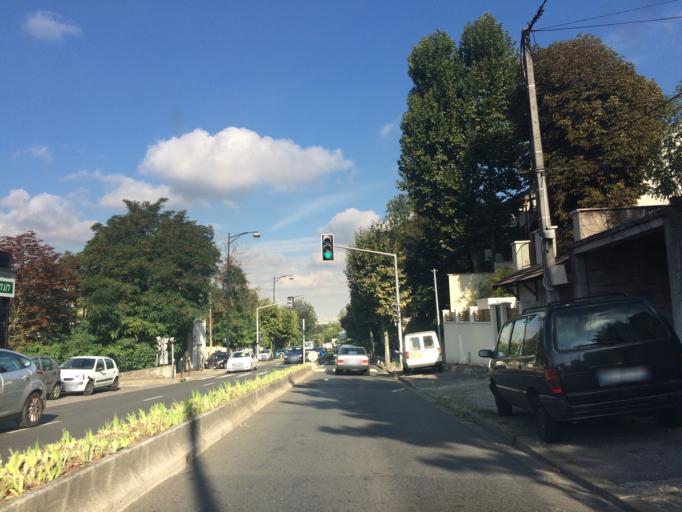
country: FR
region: Ile-de-France
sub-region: Departement du Val-de-Marne
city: Chennevieres-sur-Marne
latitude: 48.8093
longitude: 2.5232
